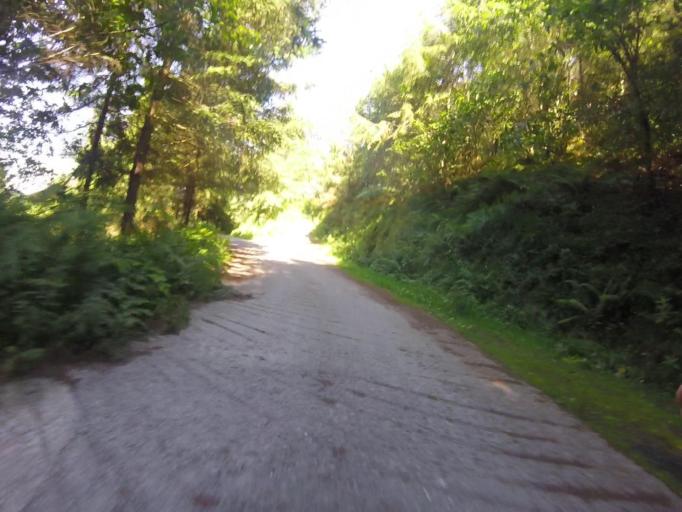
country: ES
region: Basque Country
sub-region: Provincia de Guipuzcoa
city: Irun
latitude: 43.3090
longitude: -1.7784
